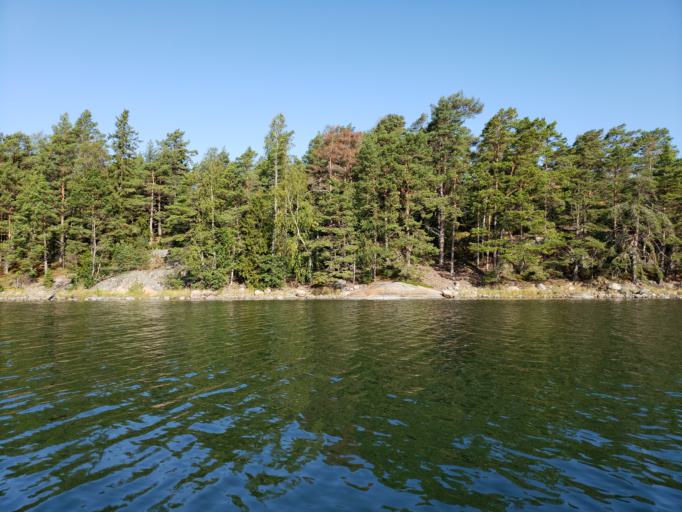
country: FI
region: Varsinais-Suomi
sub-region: Aboland-Turunmaa
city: Dragsfjaerd
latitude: 59.9149
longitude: 22.3802
